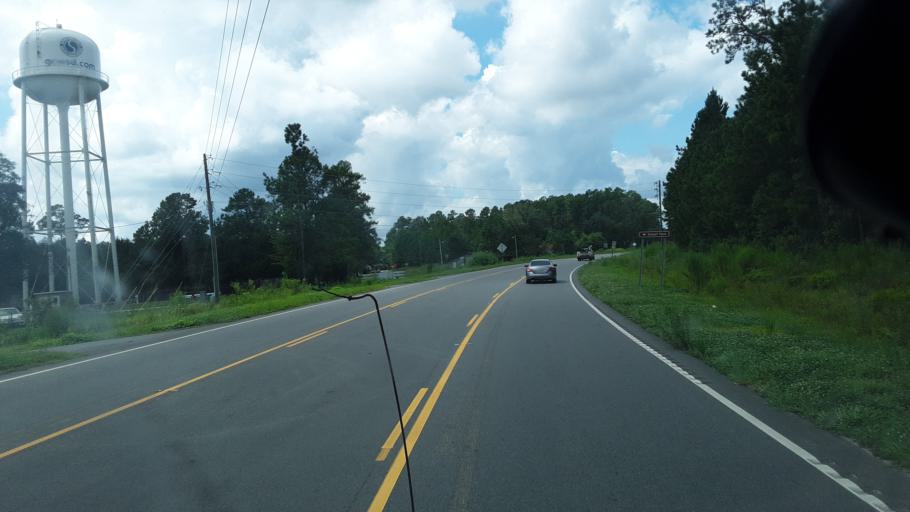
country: US
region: South Carolina
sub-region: Williamsburg County
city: Andrews
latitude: 33.3631
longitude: -79.4606
